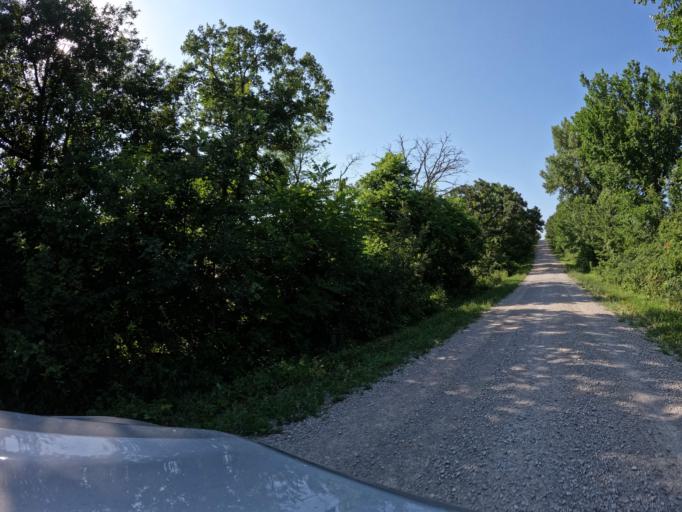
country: US
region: Iowa
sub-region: Appanoose County
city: Centerville
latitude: 40.7331
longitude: -93.0208
